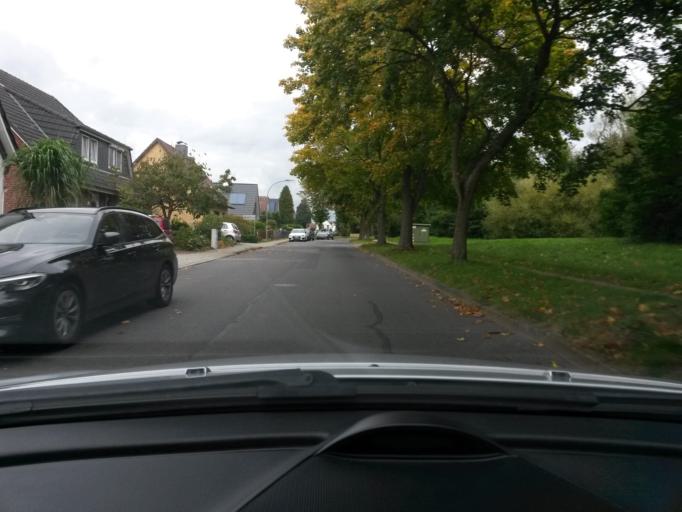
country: DE
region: Schleswig-Holstein
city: Barsbuettel
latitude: 53.5657
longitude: 10.1728
